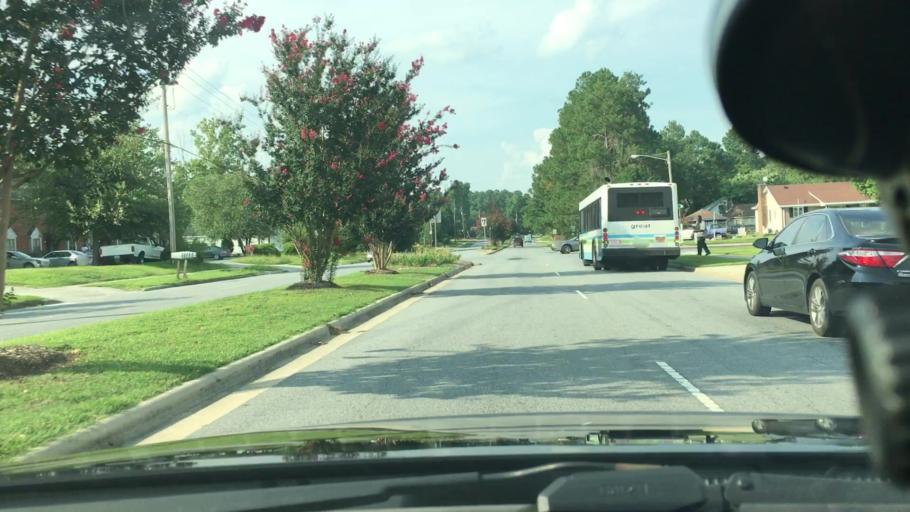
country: US
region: North Carolina
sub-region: Pitt County
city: Summerfield
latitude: 35.5799
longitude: -77.3898
